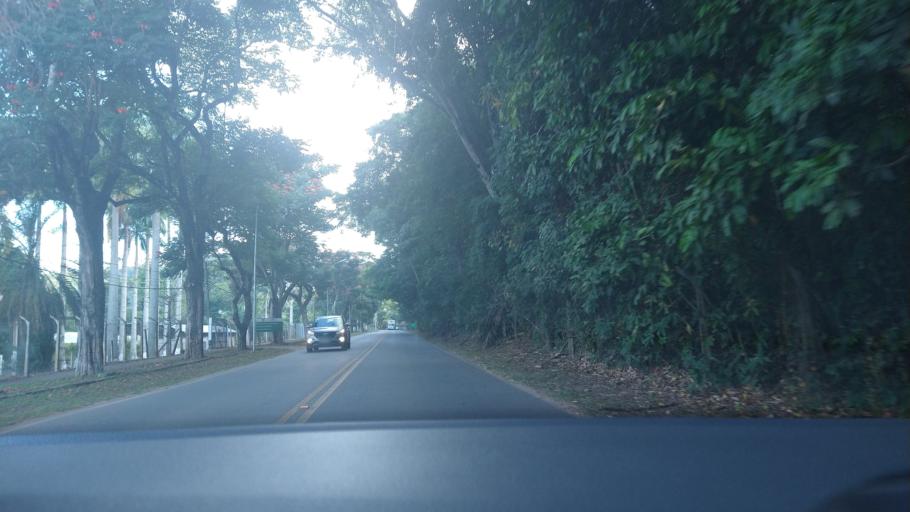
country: BR
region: Minas Gerais
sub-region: Vicosa
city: Vicosa
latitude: -20.7738
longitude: -42.8771
